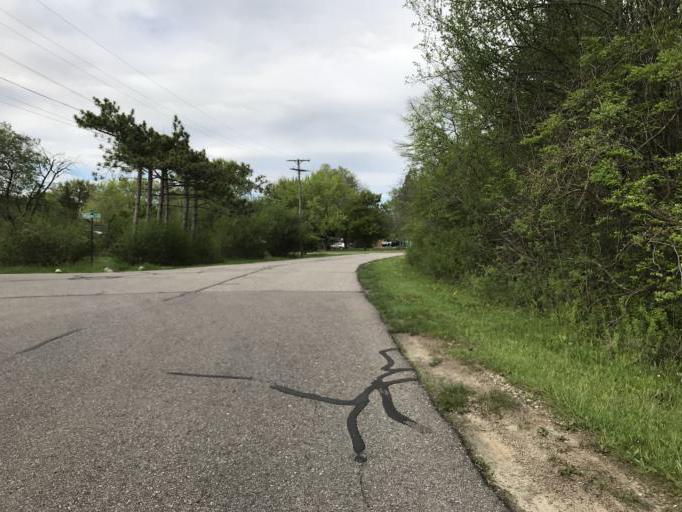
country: US
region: Michigan
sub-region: Oakland County
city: Farmington
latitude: 42.4717
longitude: -83.3299
